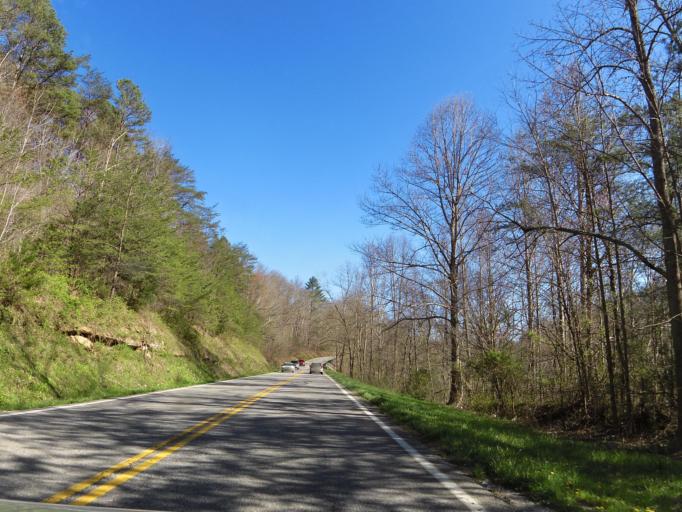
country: US
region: Tennessee
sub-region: Scott County
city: Huntsville
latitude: 36.4431
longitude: -84.4629
